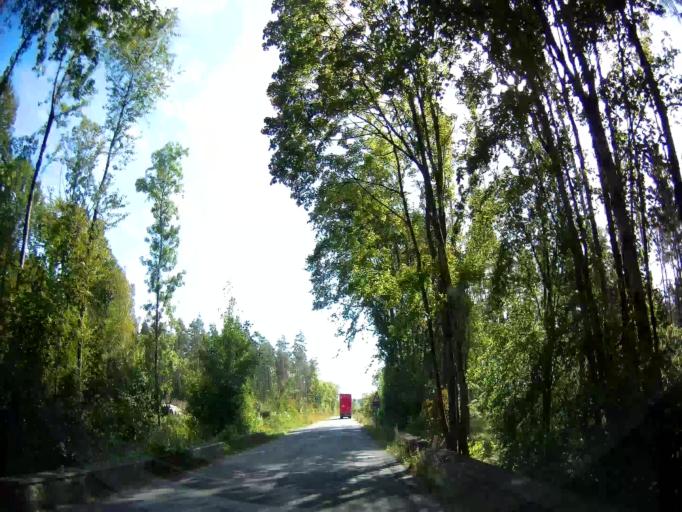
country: BE
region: Wallonia
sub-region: Province de Namur
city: Rochefort
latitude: 50.1674
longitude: 5.1786
